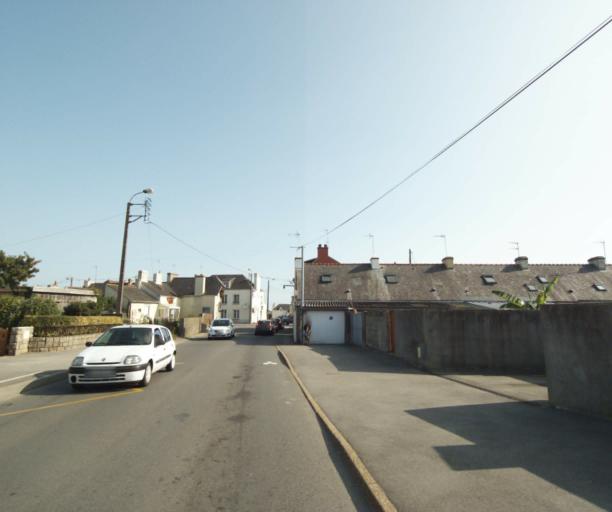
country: FR
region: Brittany
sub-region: Departement du Morbihan
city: Riantec
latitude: 47.7152
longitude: -3.3123
